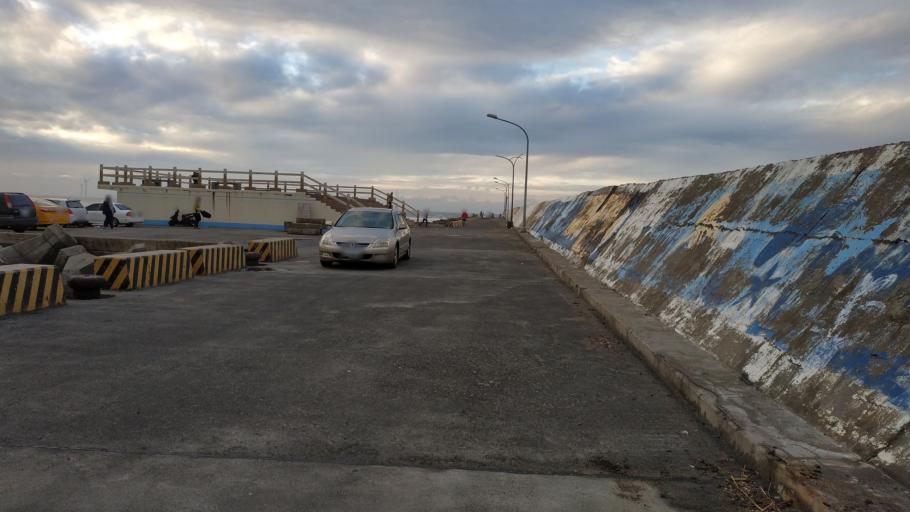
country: TW
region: Taiwan
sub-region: Miaoli
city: Miaoli
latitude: 24.7011
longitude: 120.8566
